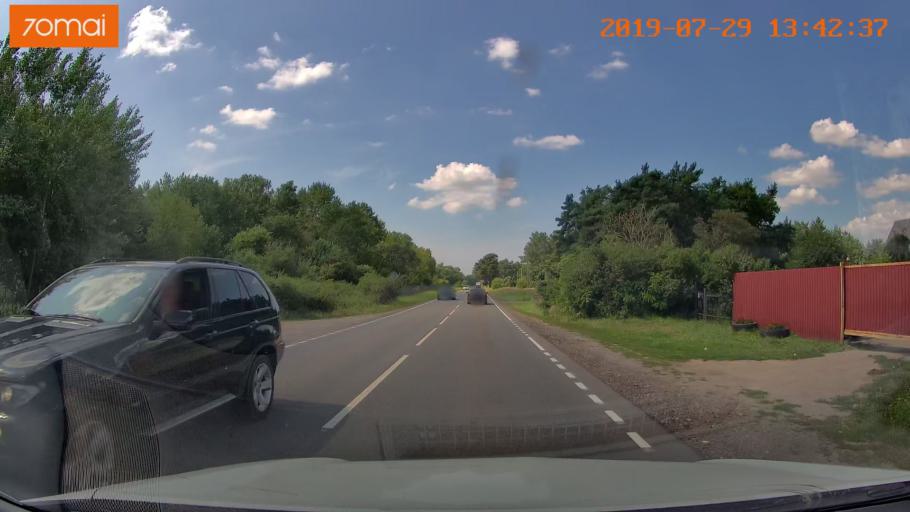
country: RU
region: Kaliningrad
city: Svetlyy
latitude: 54.7369
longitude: 20.1088
